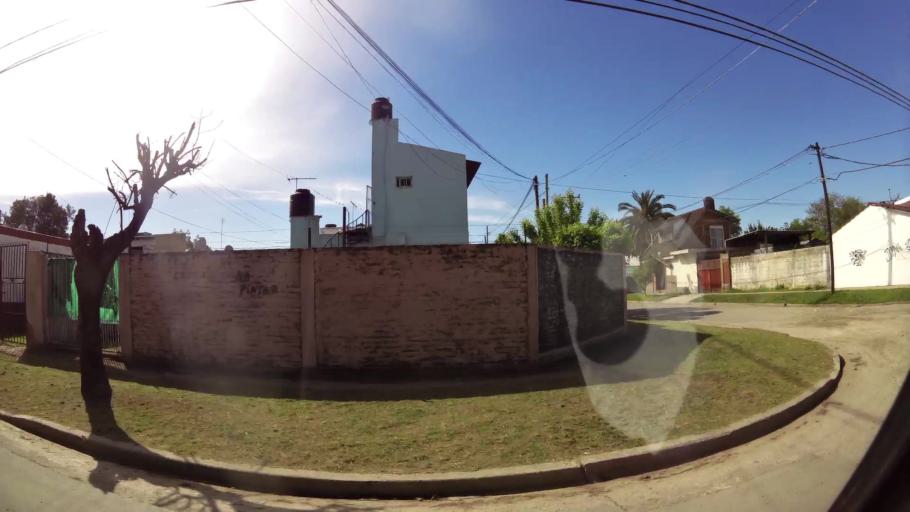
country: AR
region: Buenos Aires
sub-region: Partido de Almirante Brown
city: Adrogue
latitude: -34.8019
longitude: -58.3559
